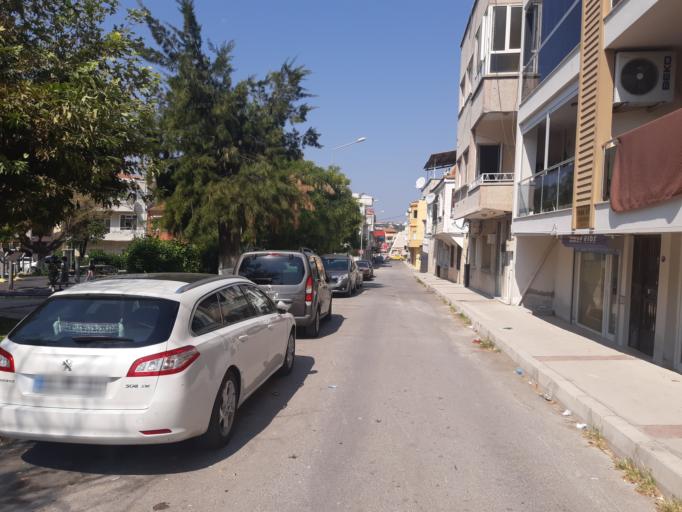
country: TR
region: Izmir
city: Urla
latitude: 38.3232
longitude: 26.7695
